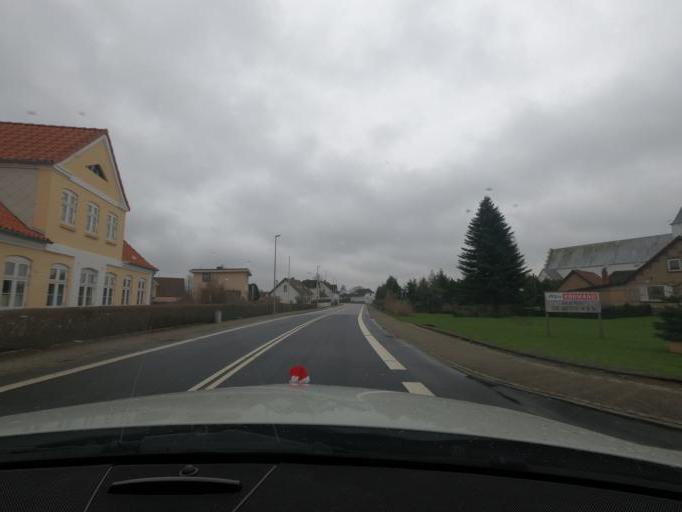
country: DK
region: South Denmark
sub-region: Haderslev Kommune
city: Starup
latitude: 55.2529
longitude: 9.6426
